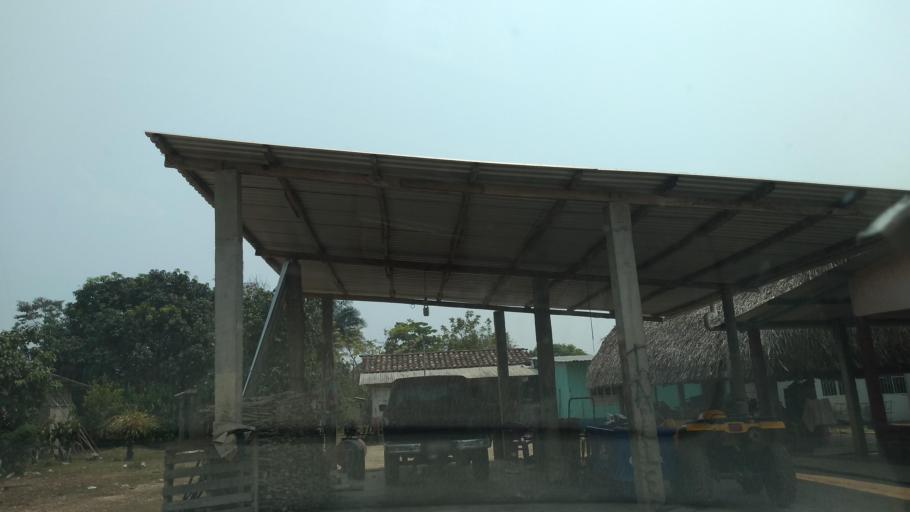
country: MX
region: Veracruz
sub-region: Tezonapa
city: Laguna Chica (Pueblo Nuevo)
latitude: 18.5329
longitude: -96.7621
